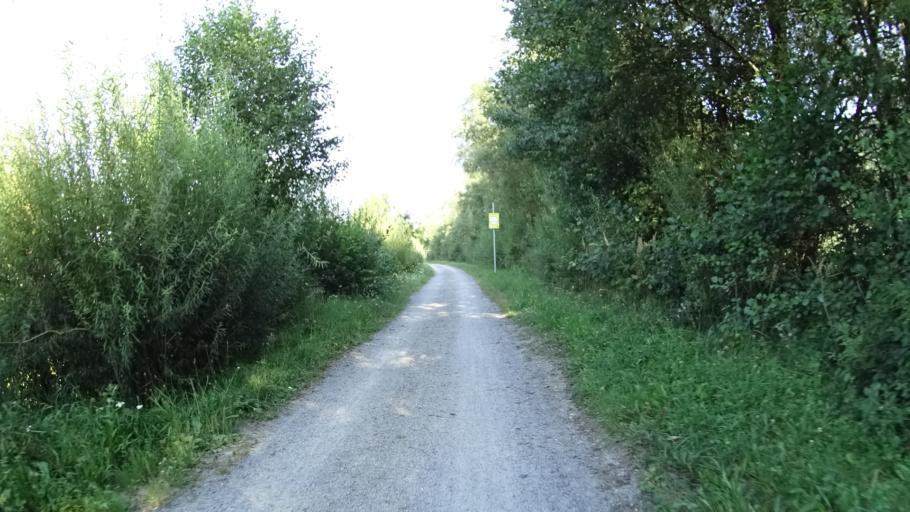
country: AT
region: Carinthia
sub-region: Politischer Bezirk Villach Land
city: Wernberg
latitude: 46.5945
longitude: 13.9617
